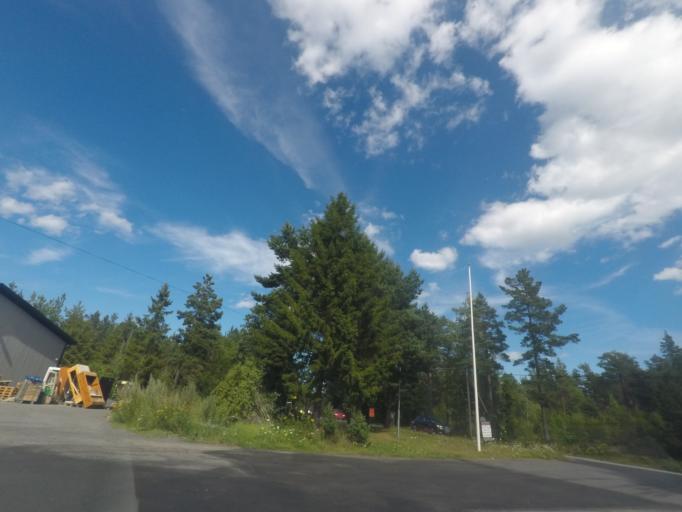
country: SE
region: Stockholm
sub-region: Norrtalje Kommun
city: Arno
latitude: 60.0928
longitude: 18.7939
